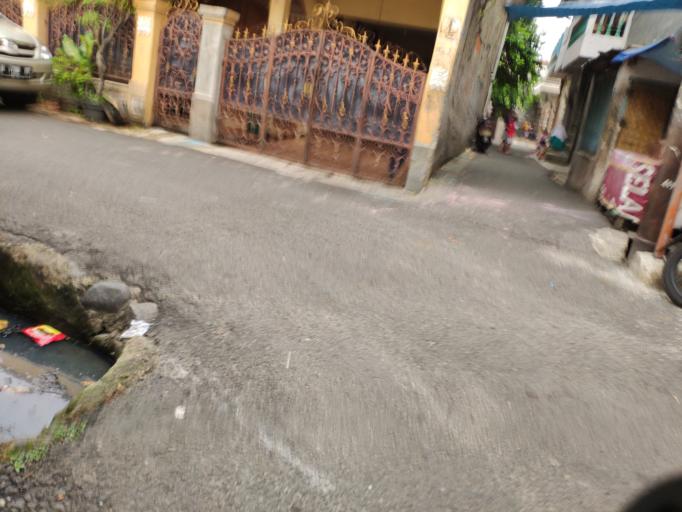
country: ID
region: Jakarta Raya
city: Jakarta
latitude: -6.1970
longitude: 106.8636
